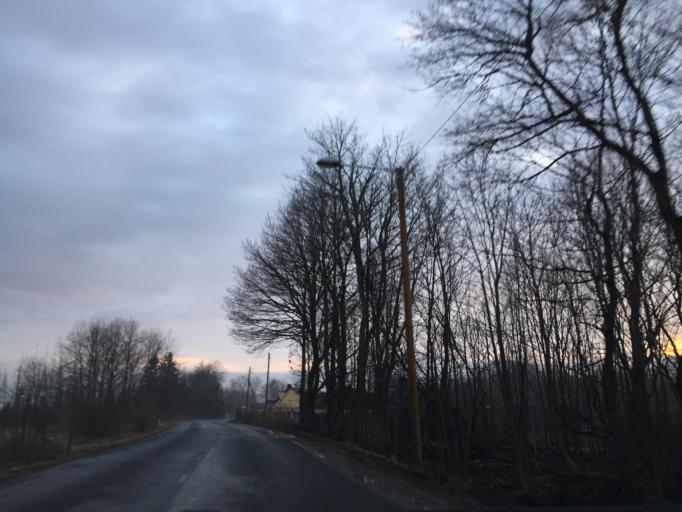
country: EE
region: Laeaene
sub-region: Lihula vald
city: Lihula
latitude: 58.6818
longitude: 23.8193
